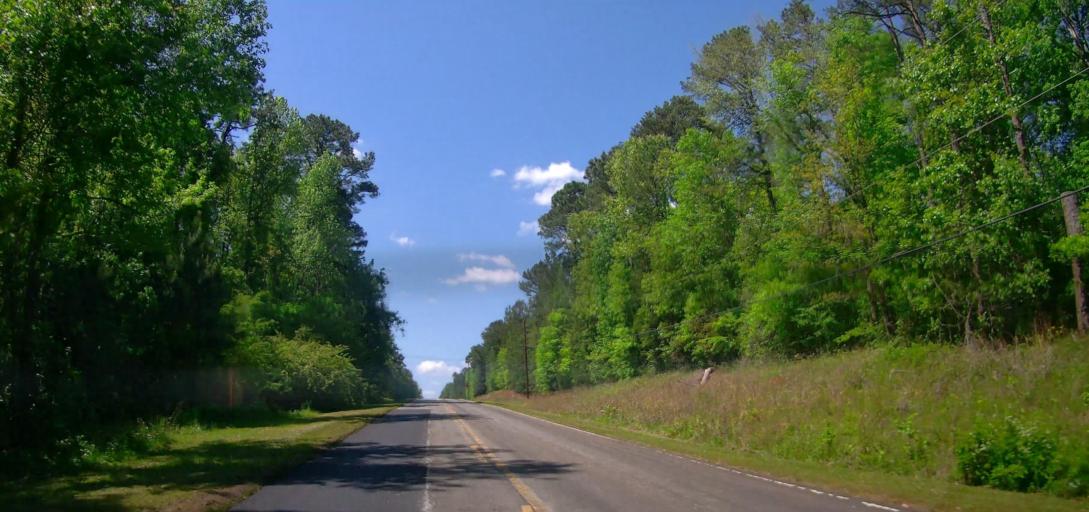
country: US
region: Georgia
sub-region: Putnam County
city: Eatonton
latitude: 33.3330
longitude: -83.4068
